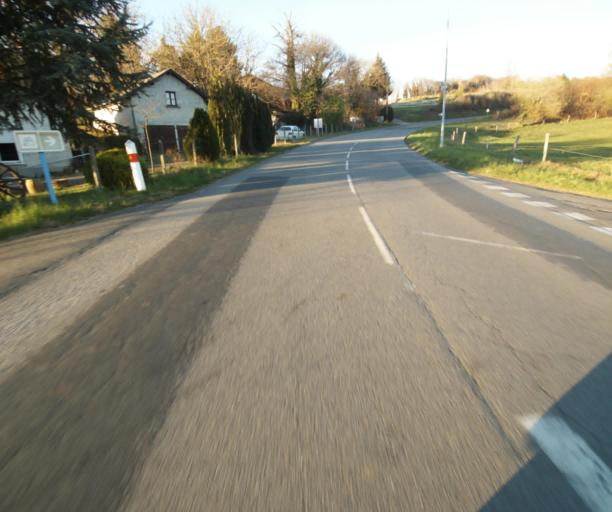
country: FR
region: Limousin
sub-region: Departement de la Correze
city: Saint-Clement
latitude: 45.3447
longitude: 1.6862
